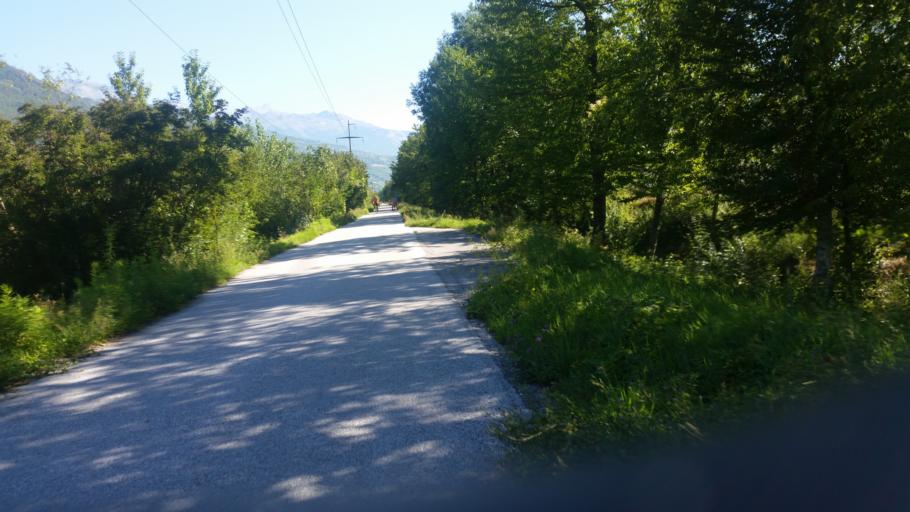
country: CH
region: Valais
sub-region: Sion District
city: Saint-Leonard
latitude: 46.2420
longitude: 7.4239
